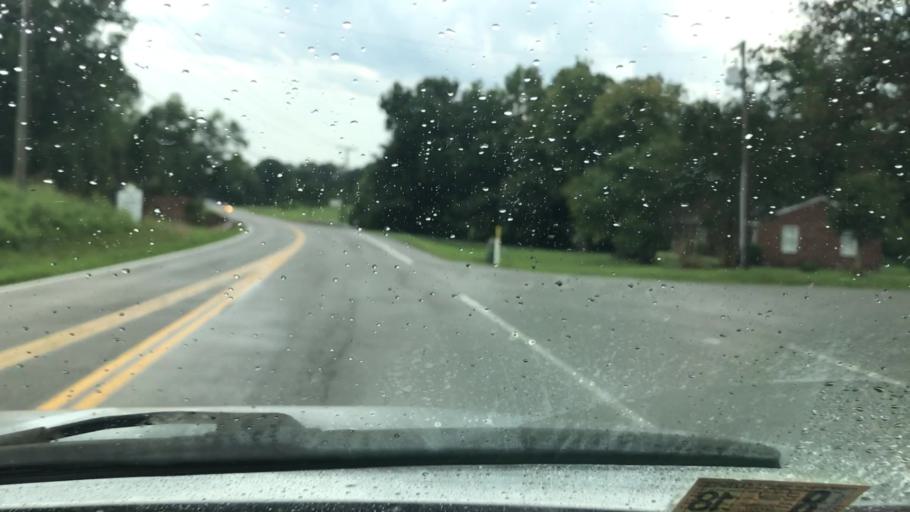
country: US
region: Virginia
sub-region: Henrico County
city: Short Pump
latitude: 37.6614
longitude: -77.6791
